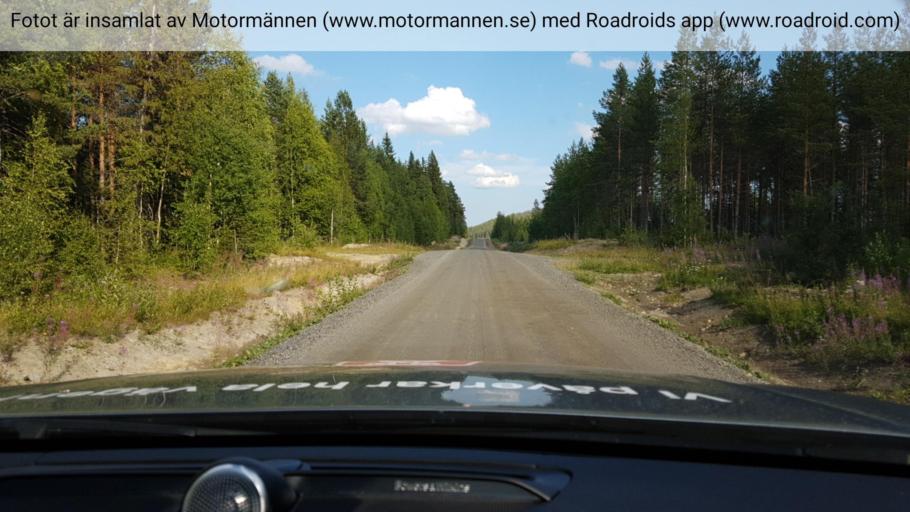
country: SE
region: Vaesterbotten
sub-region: Dorotea Kommun
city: Dorotea
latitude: 63.9196
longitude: 16.1969
